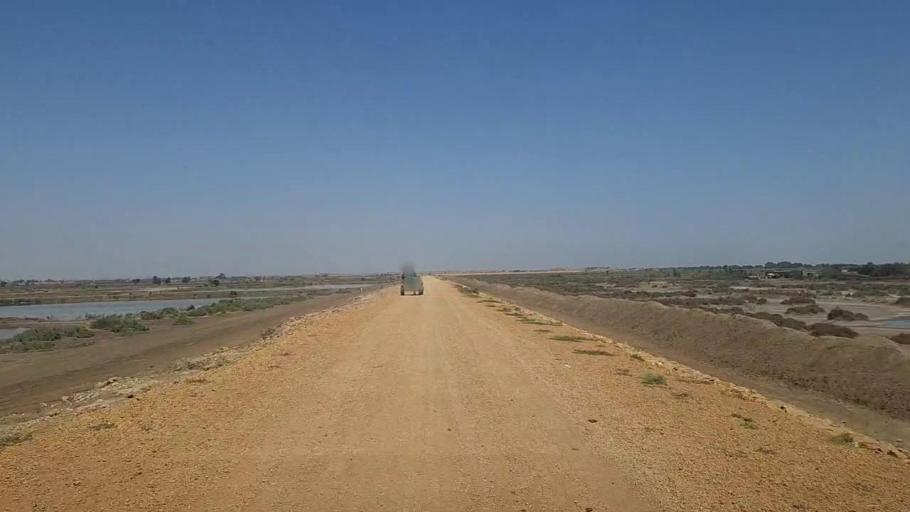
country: PK
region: Sindh
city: Thatta
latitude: 24.7893
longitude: 67.9971
